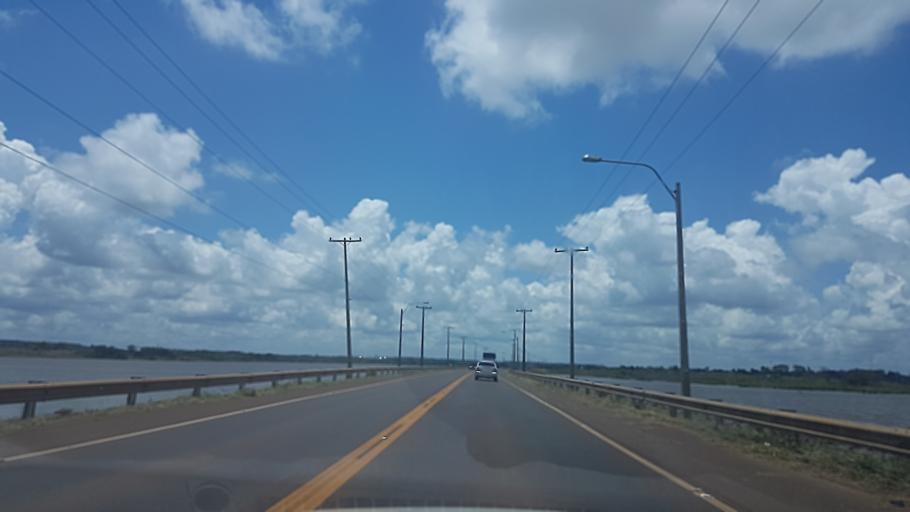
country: PY
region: Itapua
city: Carmen del Parana
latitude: -27.2071
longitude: -56.1652
